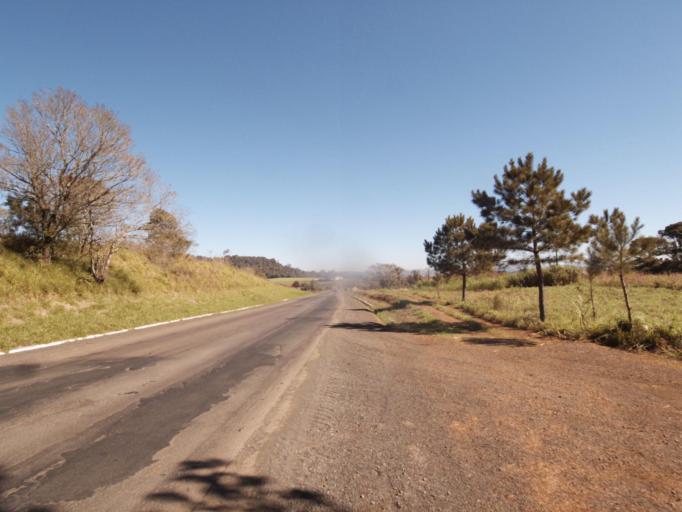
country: BR
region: Rio Grande do Sul
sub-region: Frederico Westphalen
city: Frederico Westphalen
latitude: -26.7992
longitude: -53.3492
